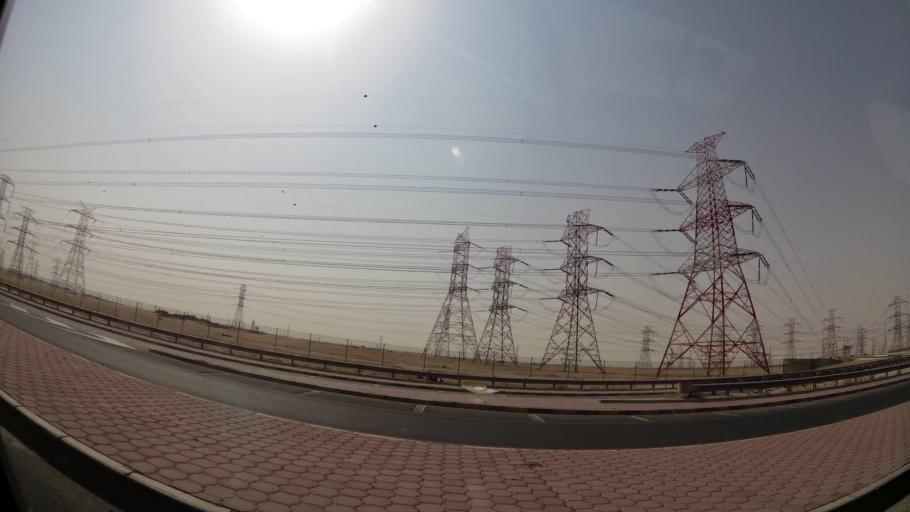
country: KW
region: Muhafazat al Jahra'
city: Al Jahra'
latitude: 29.3022
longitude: 47.6810
